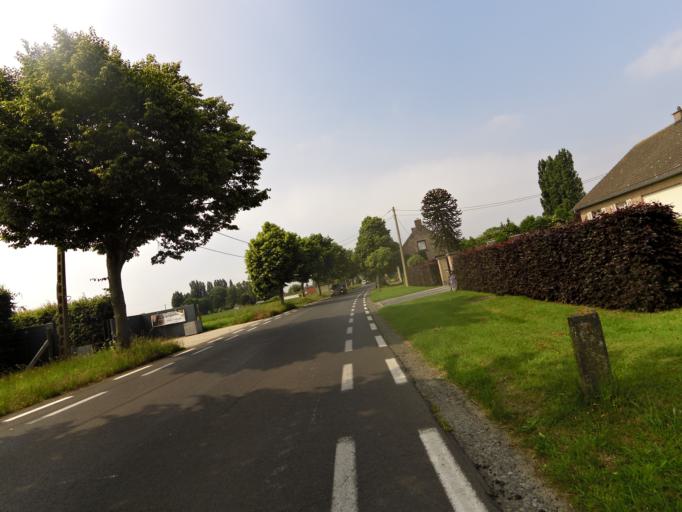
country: BE
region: Flanders
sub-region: Provincie West-Vlaanderen
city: Ichtegem
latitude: 51.1152
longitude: 3.0398
